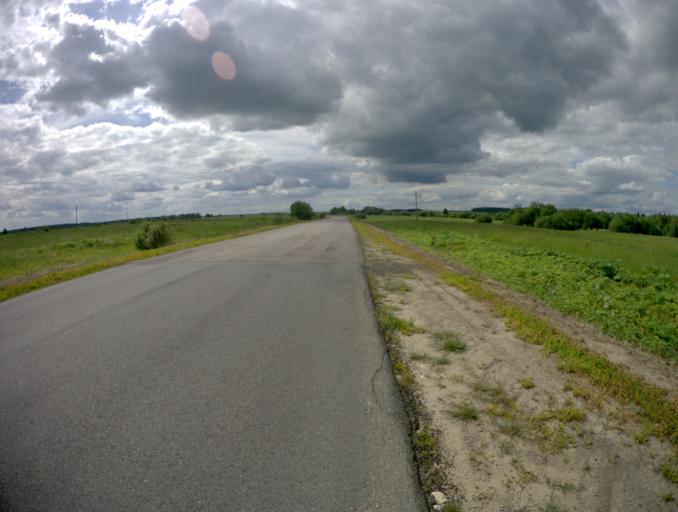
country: RU
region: Vladimir
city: Stavrovo
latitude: 56.2763
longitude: 39.8245
